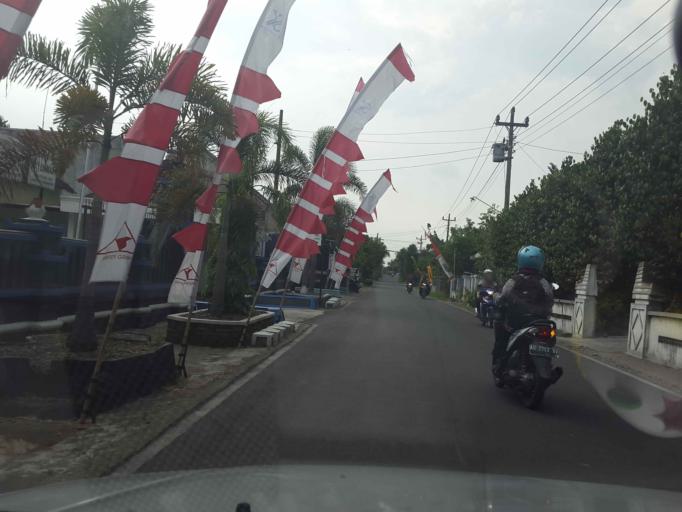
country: ID
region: Central Java
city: Jaten
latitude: -7.5534
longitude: 110.8948
